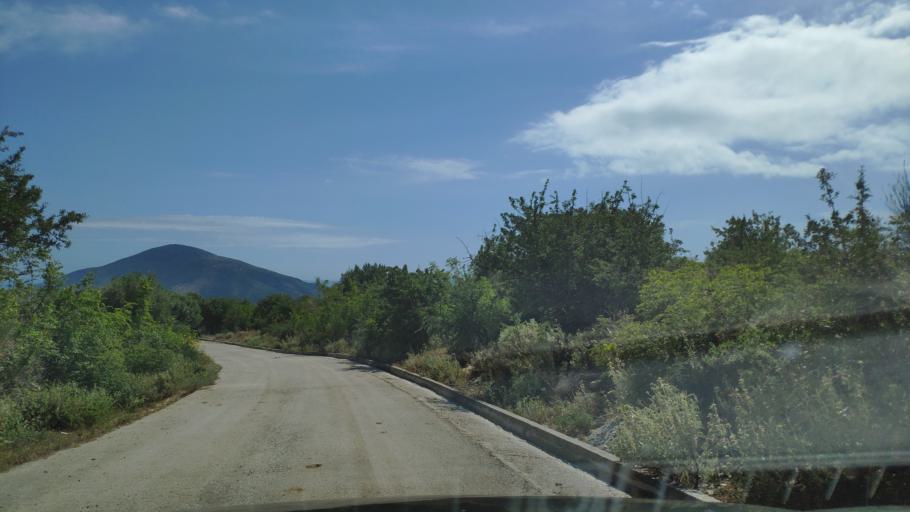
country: AL
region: Vlore
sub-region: Rrethi i Sarandes
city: Konispol
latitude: 39.6296
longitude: 20.2105
